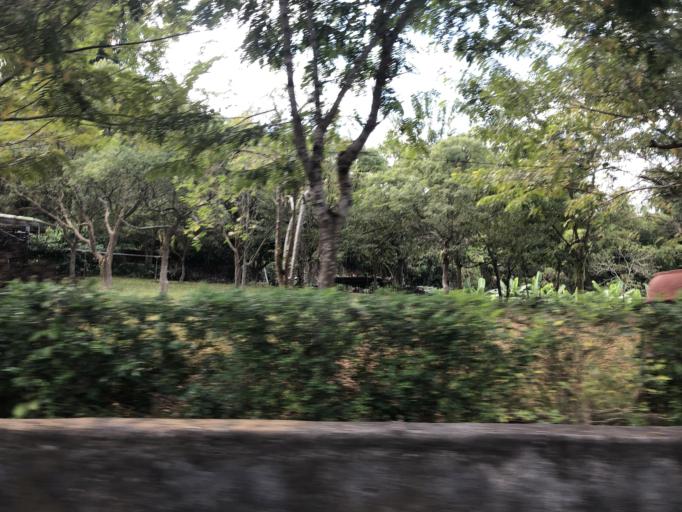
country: TW
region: Taiwan
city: Yujing
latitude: 23.0113
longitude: 120.4170
